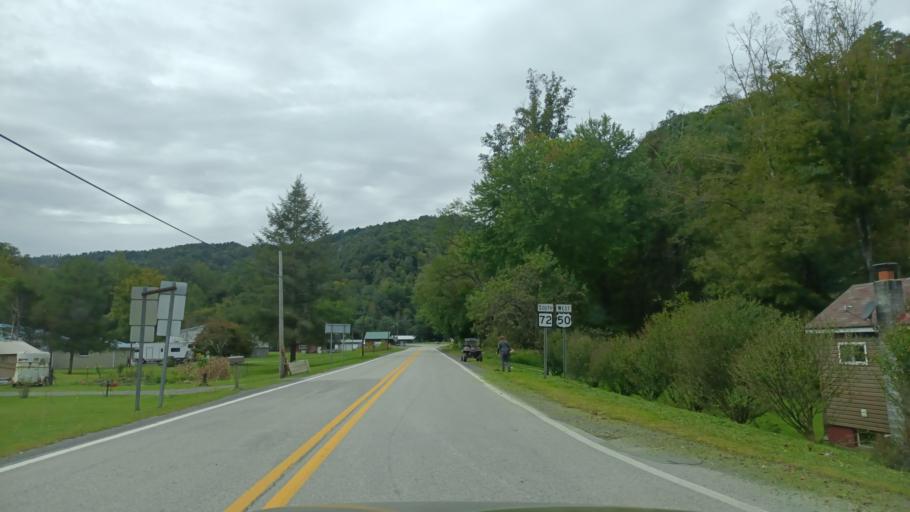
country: US
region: West Virginia
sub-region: Preston County
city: Kingwood
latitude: 39.3191
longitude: -79.6888
